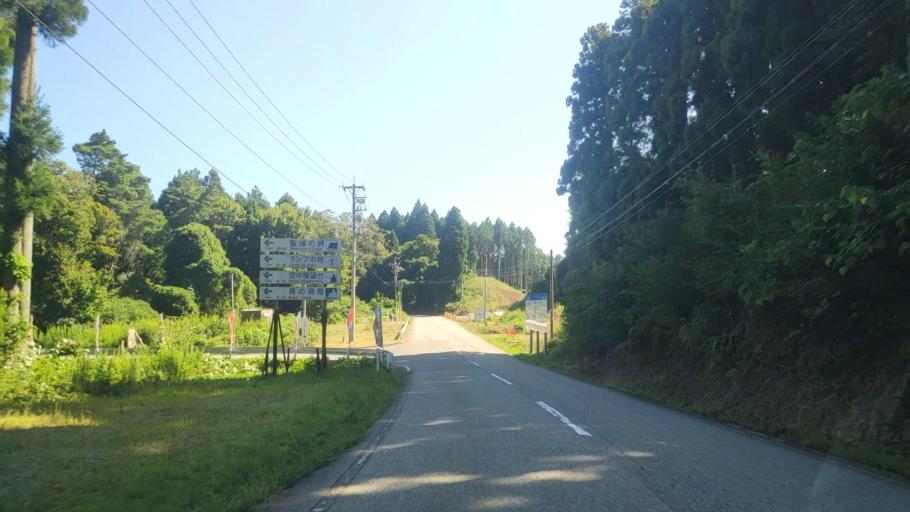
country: JP
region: Ishikawa
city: Nanao
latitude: 37.5123
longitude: 137.3361
